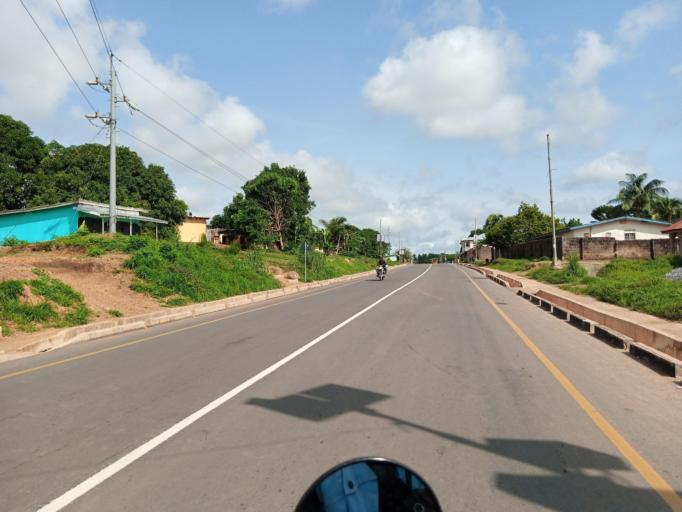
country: SL
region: Southern Province
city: Bo
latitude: 7.9498
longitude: -11.7146
